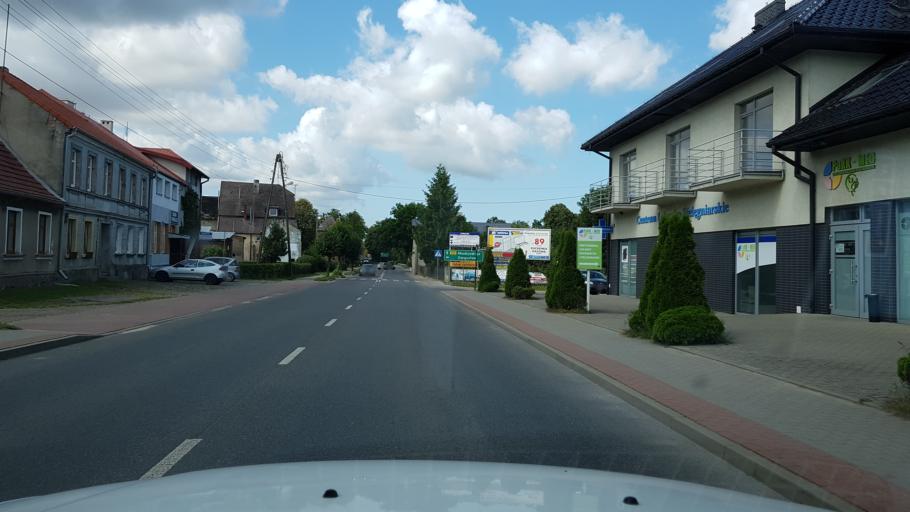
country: PL
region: West Pomeranian Voivodeship
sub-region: Powiat gryficki
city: Trzebiatow
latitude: 54.0652
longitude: 15.2797
